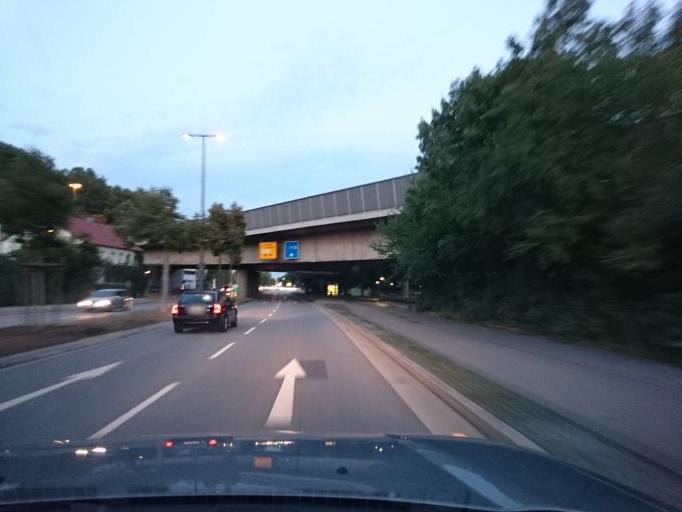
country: DE
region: Bavaria
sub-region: Upper Palatinate
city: Lappersdorf
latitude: 49.0297
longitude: 12.0780
